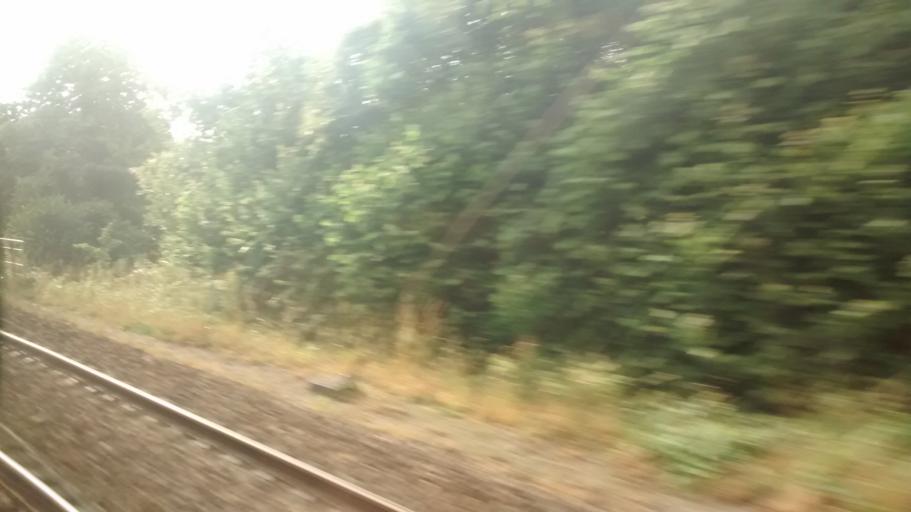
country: FR
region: Brittany
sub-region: Departement d'Ille-et-Vilaine
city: Poce-les-Bois
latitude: 48.0991
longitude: -1.2663
